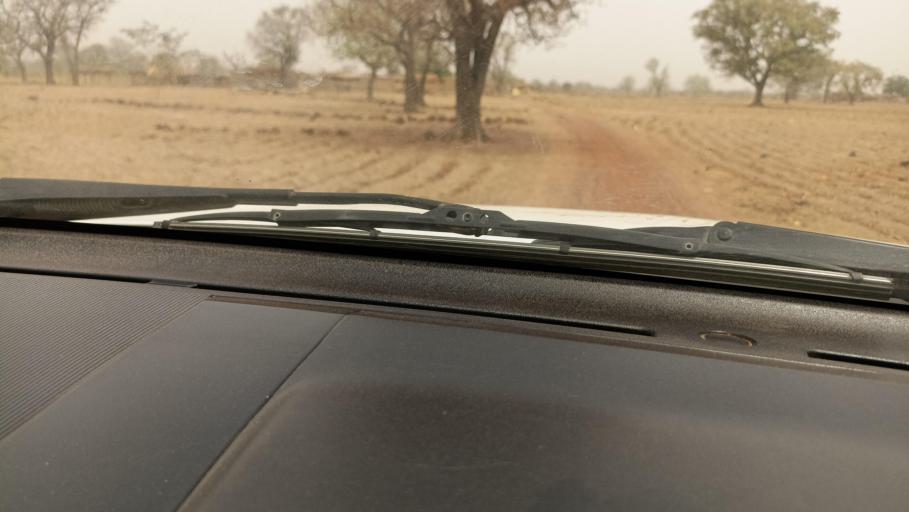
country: BF
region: Boucle du Mouhoun
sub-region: Province du Nayala
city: Toma
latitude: 12.8543
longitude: -2.7952
